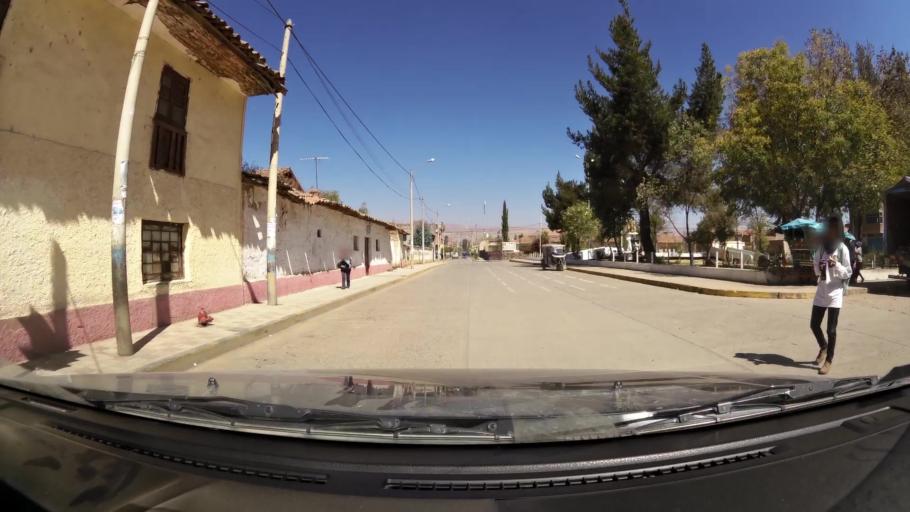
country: PE
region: Junin
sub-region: Provincia de Concepcion
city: Concepcion
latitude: -11.9138
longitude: -75.3158
